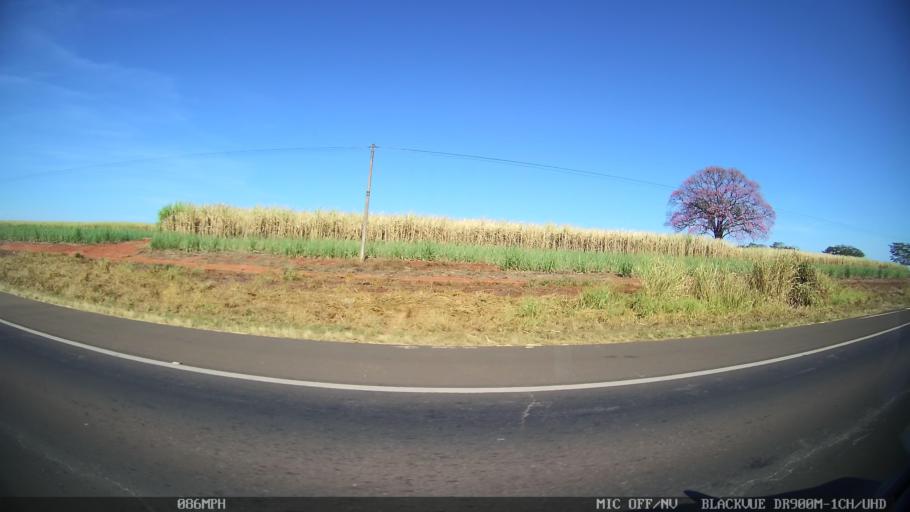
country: BR
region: Sao Paulo
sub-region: Olimpia
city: Olimpia
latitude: -20.6703
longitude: -48.8749
